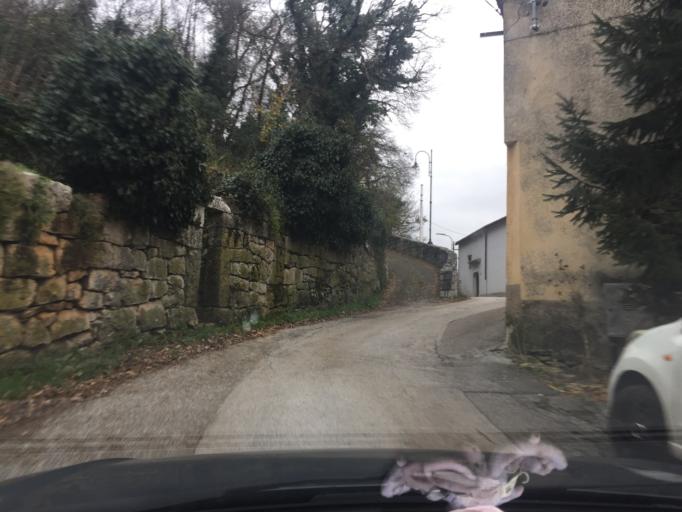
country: IT
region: Friuli Venezia Giulia
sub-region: Provincia di Trieste
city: Zolla
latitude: 45.7198
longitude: 13.8036
